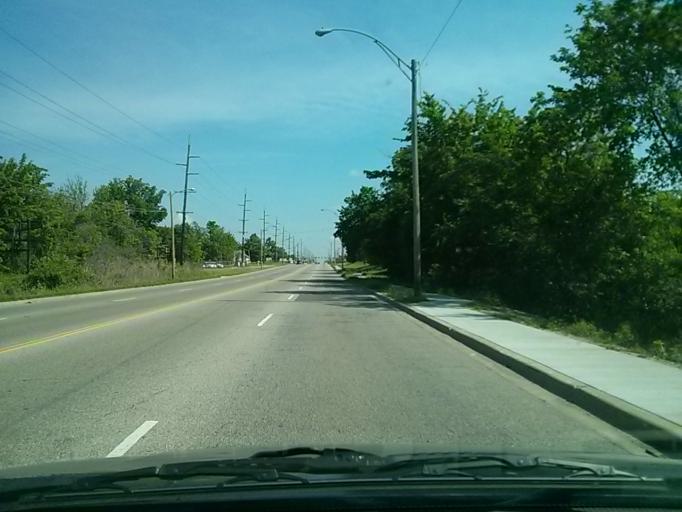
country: US
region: Oklahoma
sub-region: Tulsa County
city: Turley
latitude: 36.2151
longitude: -95.9755
